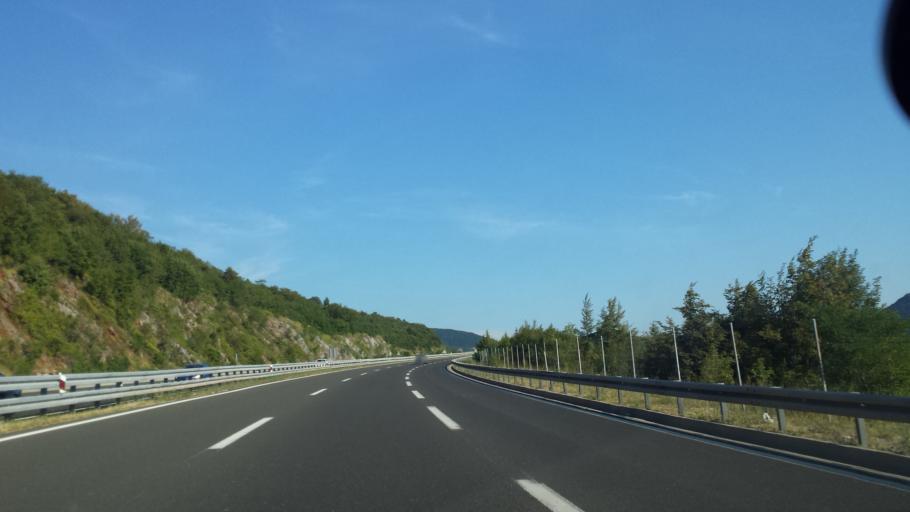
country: HR
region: Primorsko-Goranska
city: Krasica
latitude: 45.3596
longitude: 14.5757
